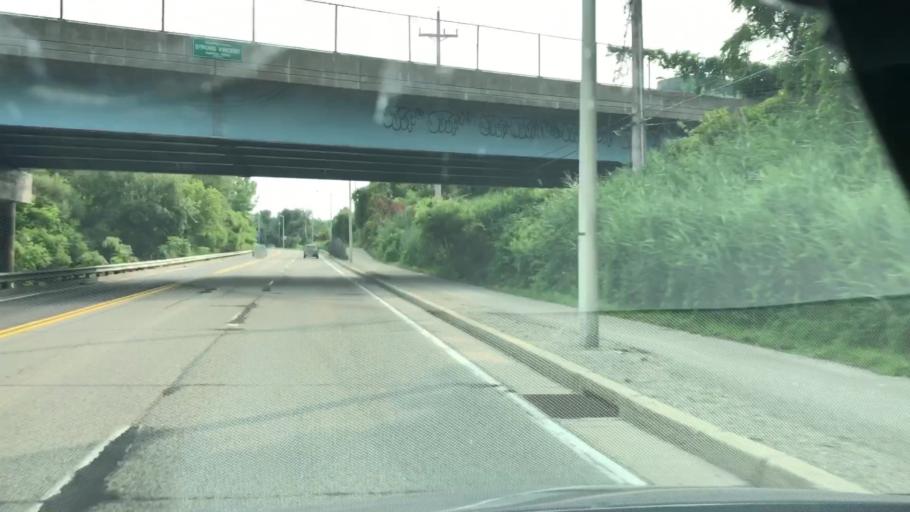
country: US
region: Pennsylvania
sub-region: Erie County
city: Erie
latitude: 42.1198
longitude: -80.1141
